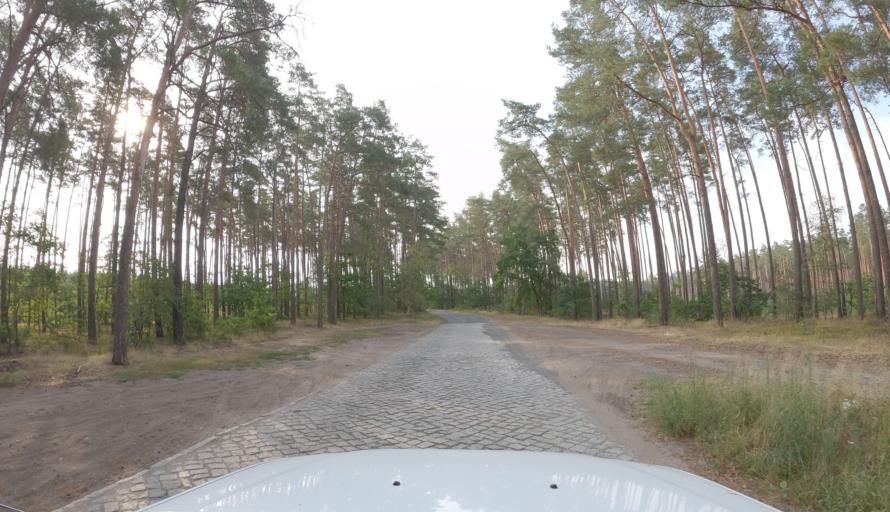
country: PL
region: West Pomeranian Voivodeship
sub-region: Powiat stargardzki
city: Kobylanka
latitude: 53.4373
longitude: 14.8912
